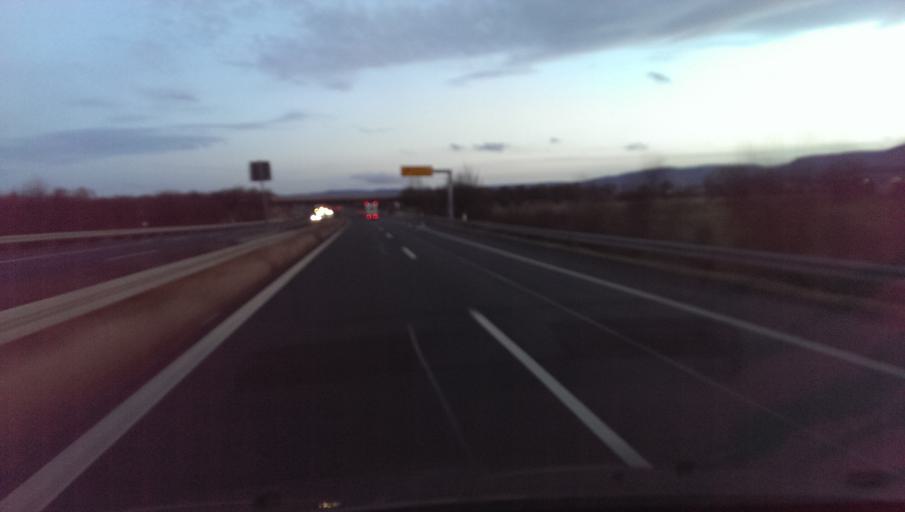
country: DE
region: Saxony-Anhalt
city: Veckenstedt
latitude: 51.8900
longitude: 10.7119
